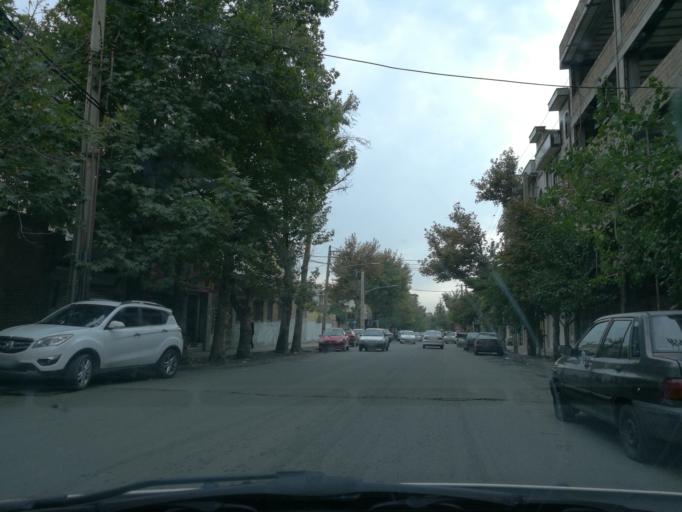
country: IR
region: Alborz
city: Karaj
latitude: 35.8557
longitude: 50.9531
